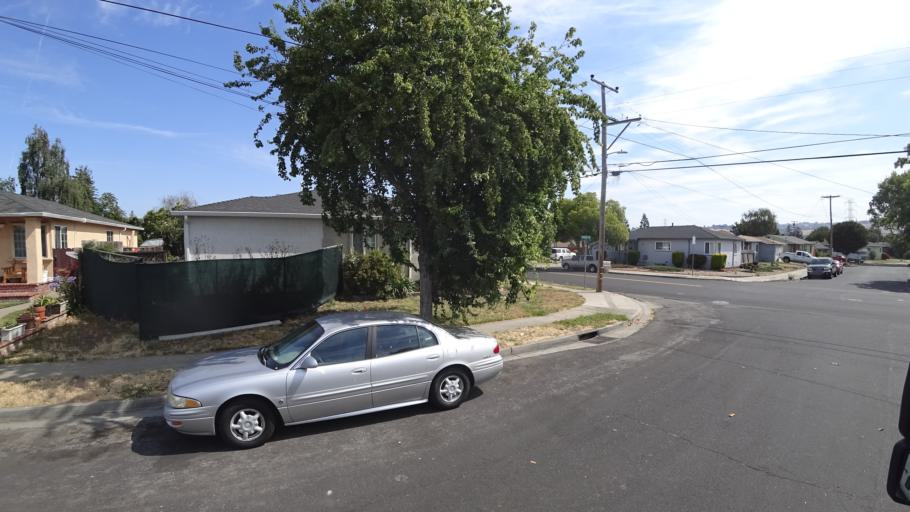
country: US
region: California
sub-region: Alameda County
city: Hayward
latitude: 37.6447
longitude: -122.0910
